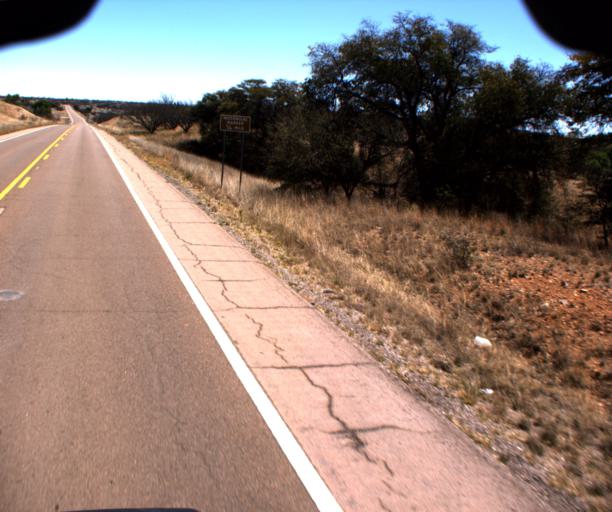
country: US
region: Arizona
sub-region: Pima County
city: Corona de Tucson
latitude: 31.6574
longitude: -110.7017
